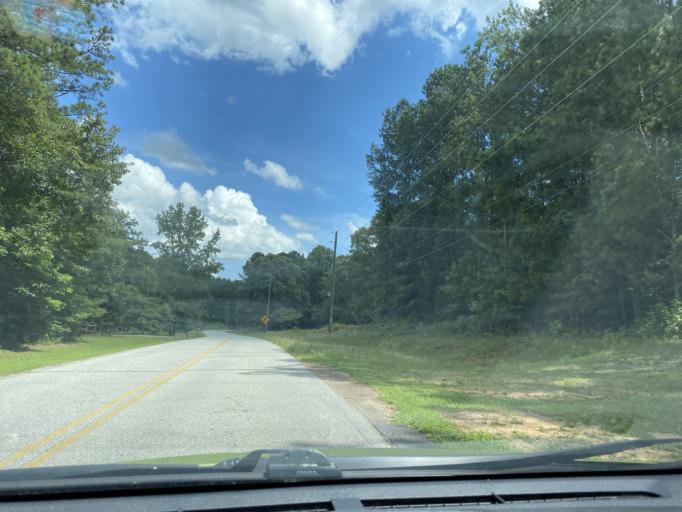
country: US
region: Georgia
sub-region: Fayette County
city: Peachtree City
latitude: 33.4140
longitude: -84.6940
